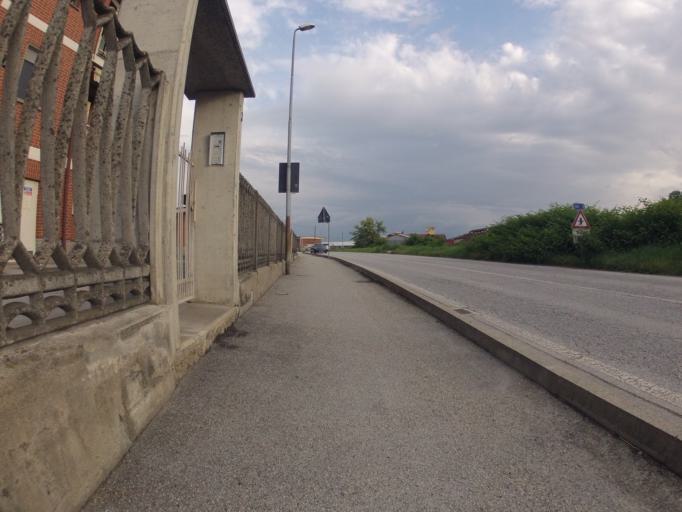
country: IT
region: Piedmont
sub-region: Provincia di Cuneo
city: Moretta
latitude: 44.7621
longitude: 7.5321
